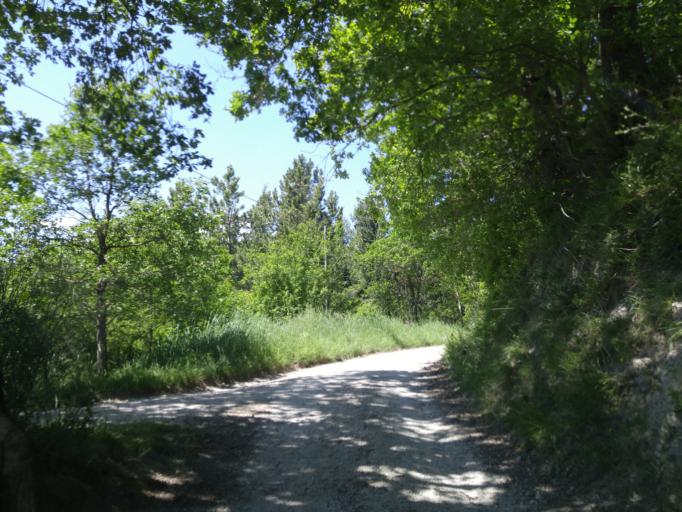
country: IT
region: The Marches
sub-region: Provincia di Pesaro e Urbino
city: Canavaccio
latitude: 43.7157
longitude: 12.6865
